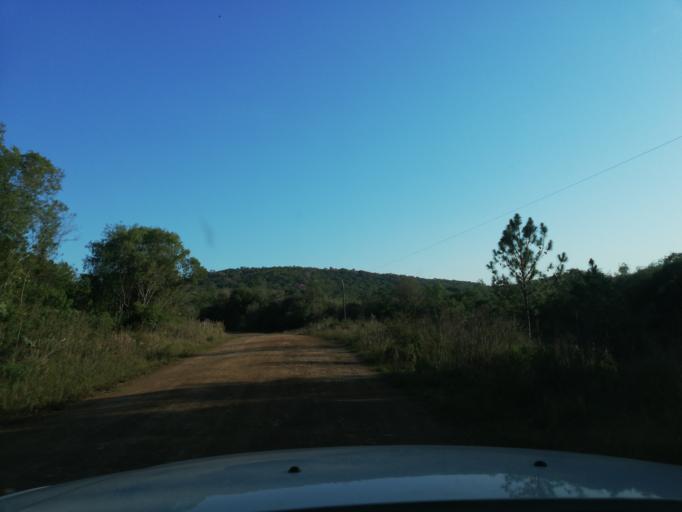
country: AR
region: Misiones
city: Cerro Cora
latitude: -27.6073
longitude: -55.7040
